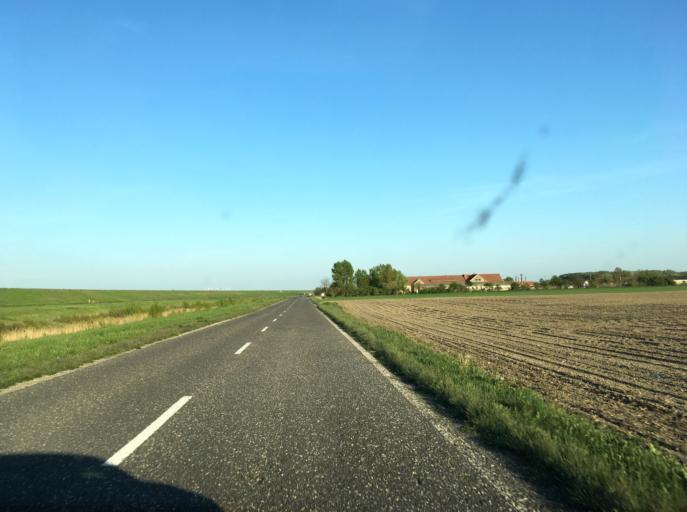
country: SK
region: Trnavsky
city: Samorin
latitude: 47.9900
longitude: 17.3580
